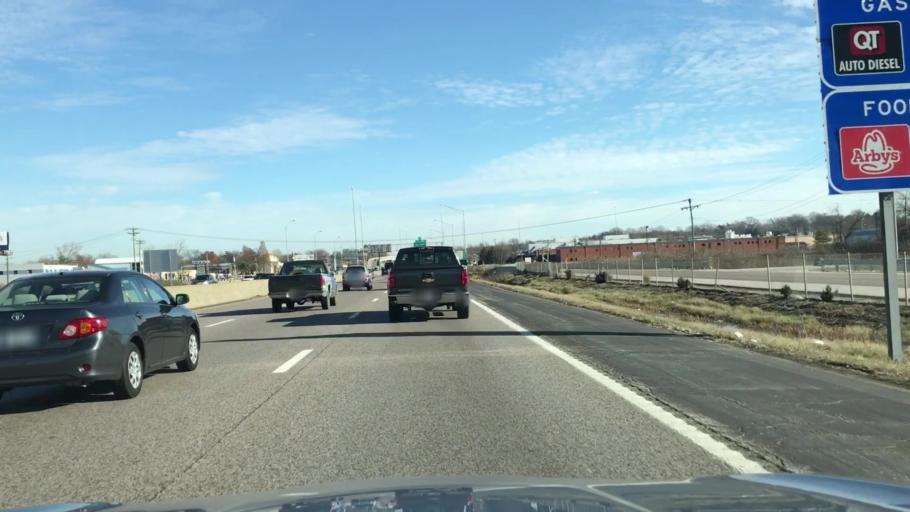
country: US
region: Missouri
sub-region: Saint Louis County
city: Hazelwood
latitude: 38.7772
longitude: -90.3521
